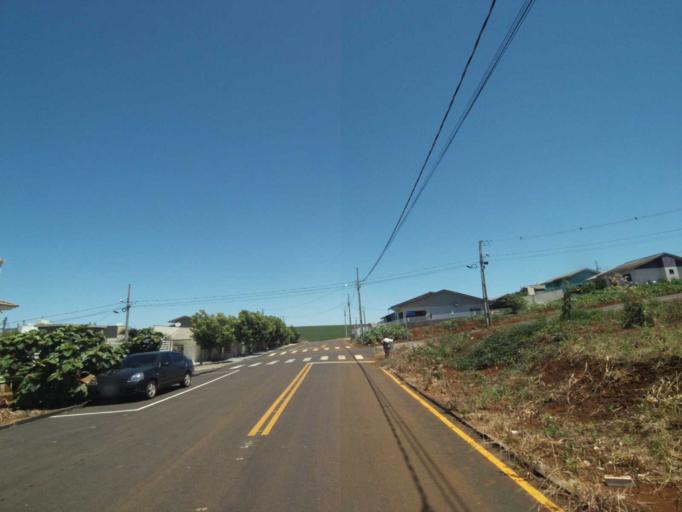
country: BR
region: Parana
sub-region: Coronel Vivida
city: Coronel Vivida
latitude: -25.9818
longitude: -52.8155
